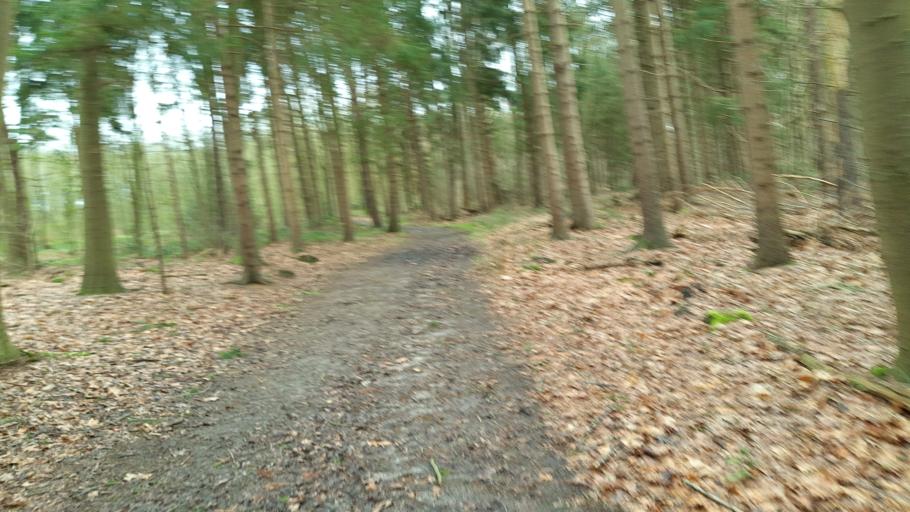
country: NL
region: Drenthe
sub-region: Gemeente Assen
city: Assen
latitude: 52.8480
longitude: 6.5917
